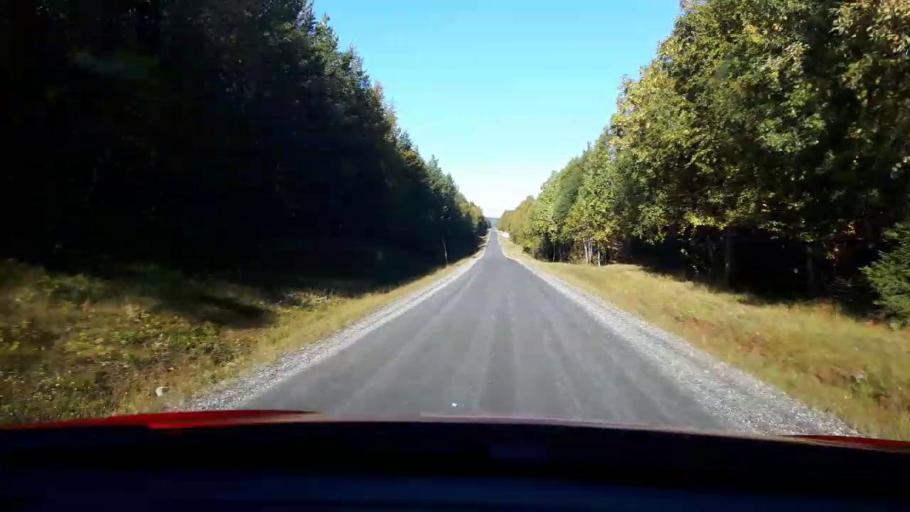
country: NO
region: Nord-Trondelag
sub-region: Lierne
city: Sandvika
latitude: 64.5395
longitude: 14.0050
